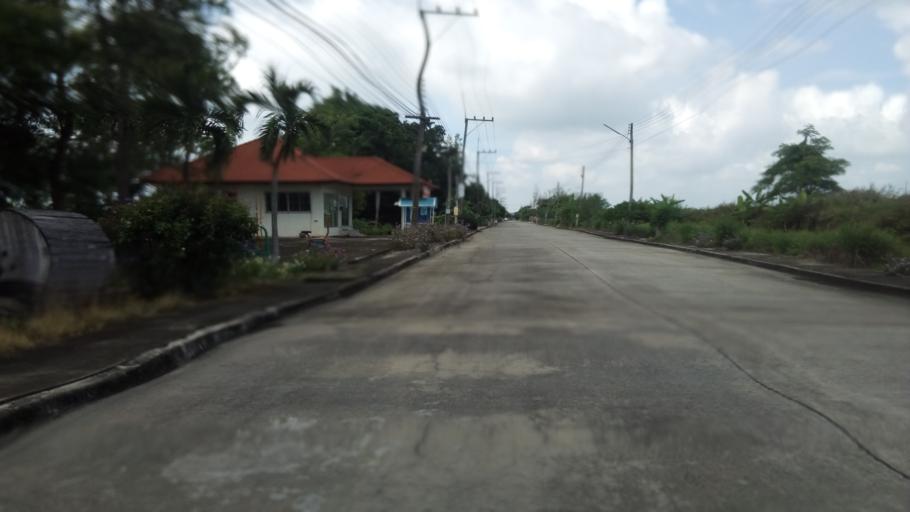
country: TH
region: Pathum Thani
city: Nong Suea
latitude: 14.0567
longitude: 100.8602
